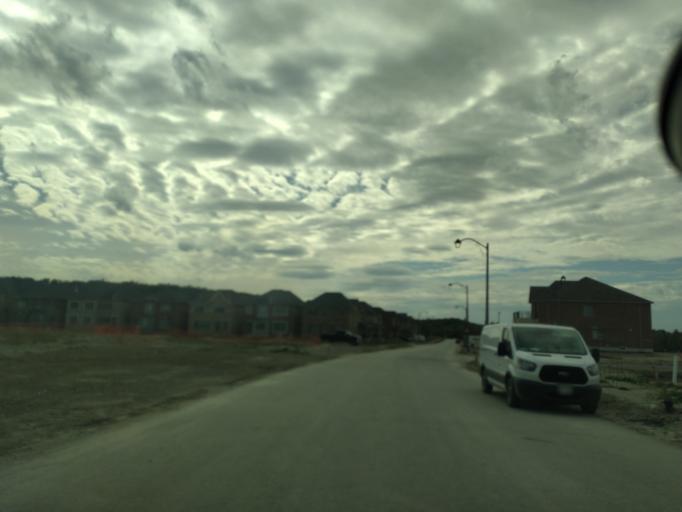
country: CA
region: Ontario
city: Newmarket
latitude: 44.0984
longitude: -79.5052
